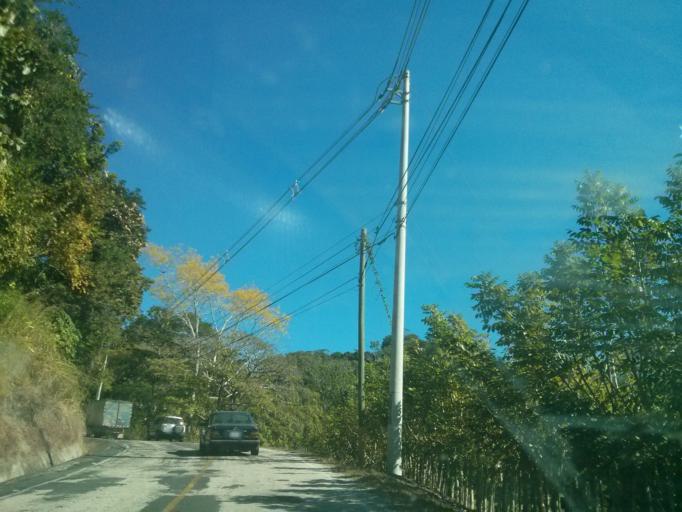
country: CR
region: Puntarenas
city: Paquera
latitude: 9.7883
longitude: -84.9413
